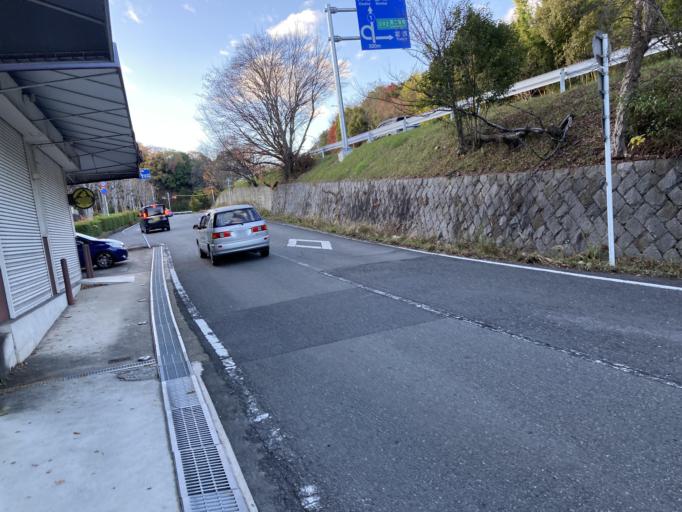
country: JP
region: Nara
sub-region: Ikoma-shi
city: Ikoma
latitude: 34.6878
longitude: 135.7252
